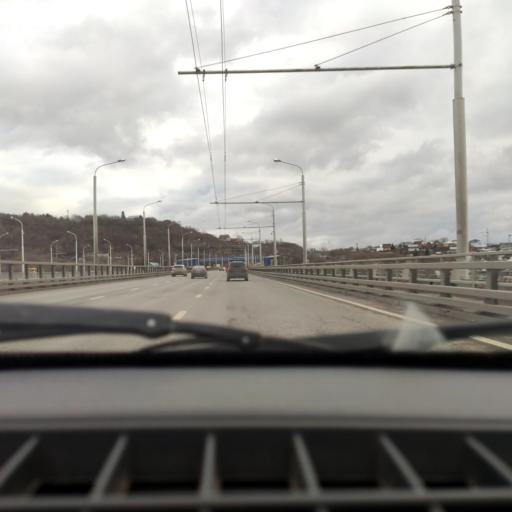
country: RU
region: Bashkortostan
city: Ufa
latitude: 54.7569
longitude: 55.9648
